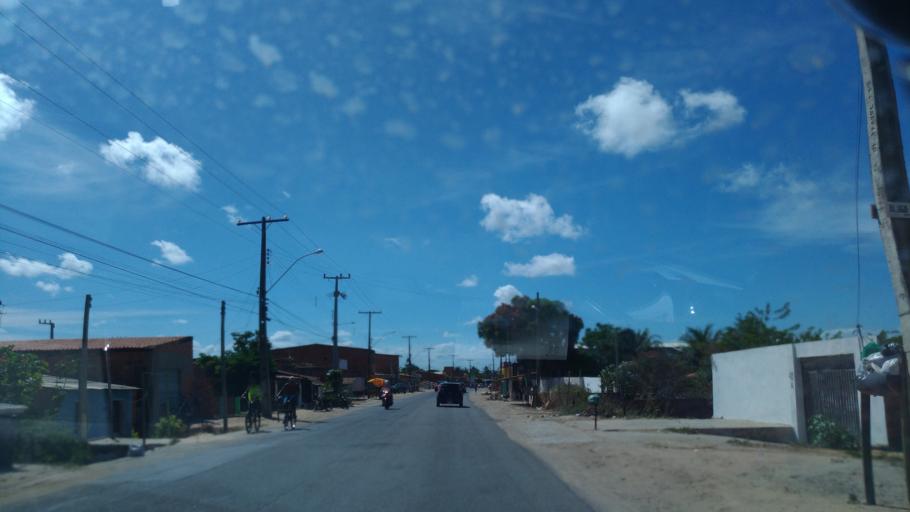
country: BR
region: Alagoas
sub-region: Marechal Deodoro
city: Marechal Deodoro
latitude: -9.7615
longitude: -35.8644
